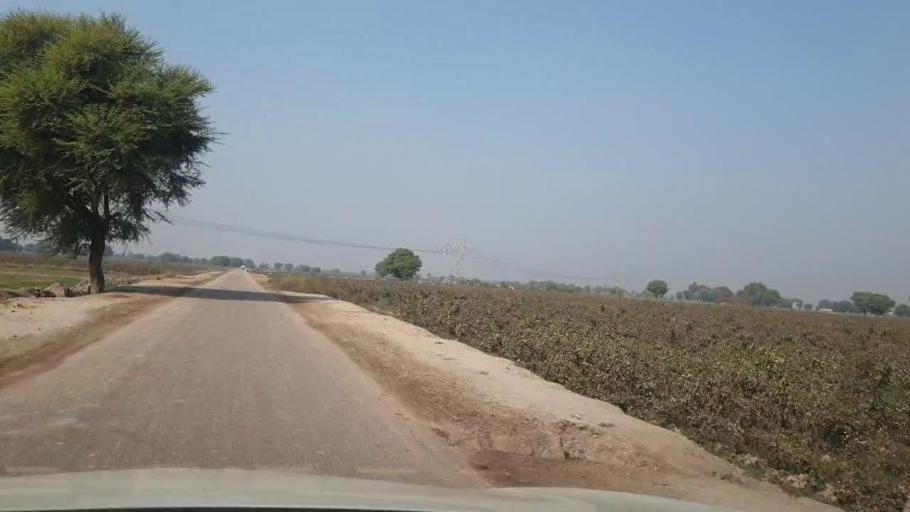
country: PK
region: Sindh
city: Bhan
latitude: 26.5330
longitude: 67.7509
